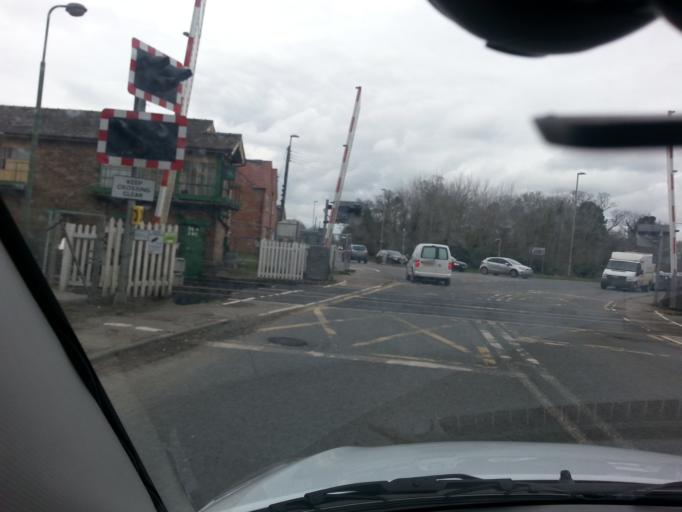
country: GB
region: England
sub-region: Norfolk
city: Weeting
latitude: 52.4537
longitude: 0.6225
